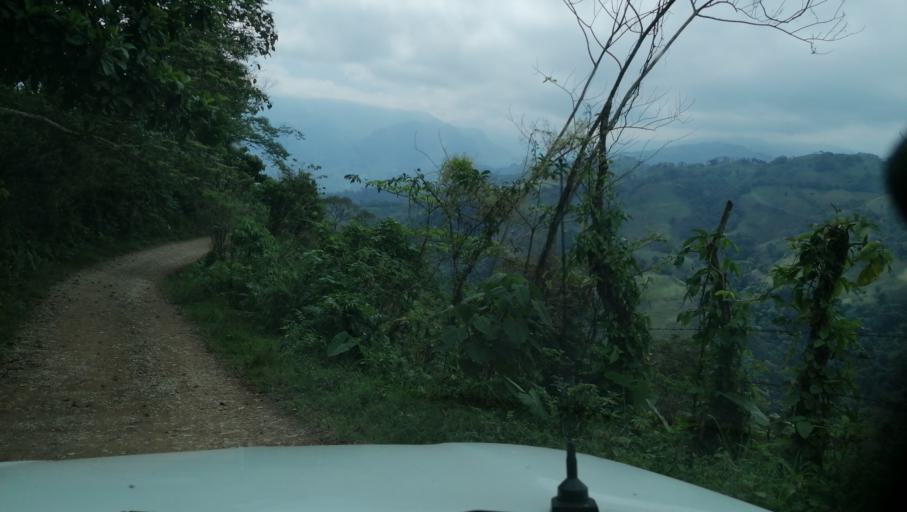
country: MX
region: Chiapas
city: Ixtacomitan
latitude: 17.3591
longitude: -93.1226
